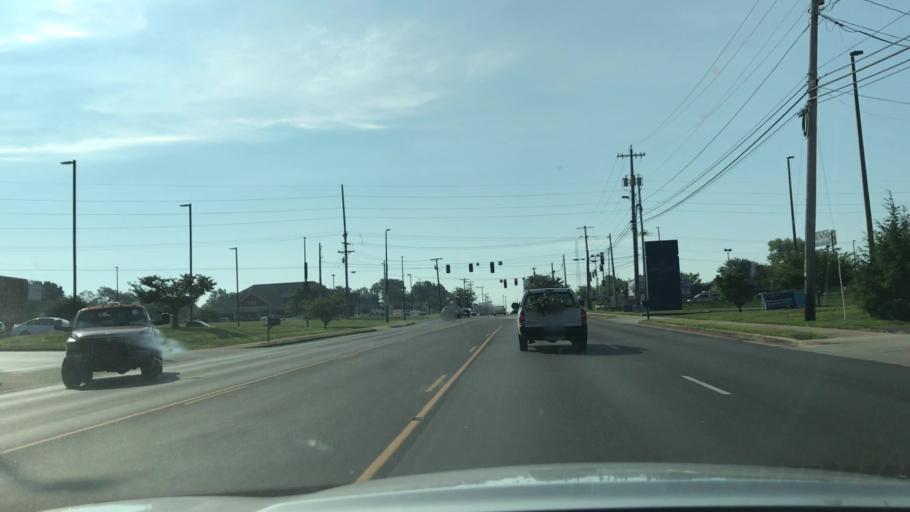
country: US
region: Kentucky
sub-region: Barren County
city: Glasgow
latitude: 37.0028
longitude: -85.9277
